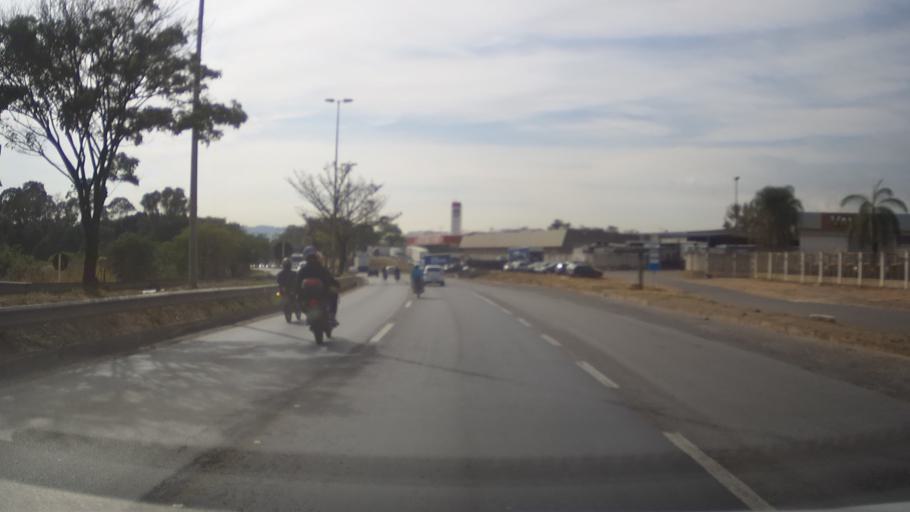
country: BR
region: Minas Gerais
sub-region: Contagem
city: Contagem
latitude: -19.9217
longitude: -44.0228
